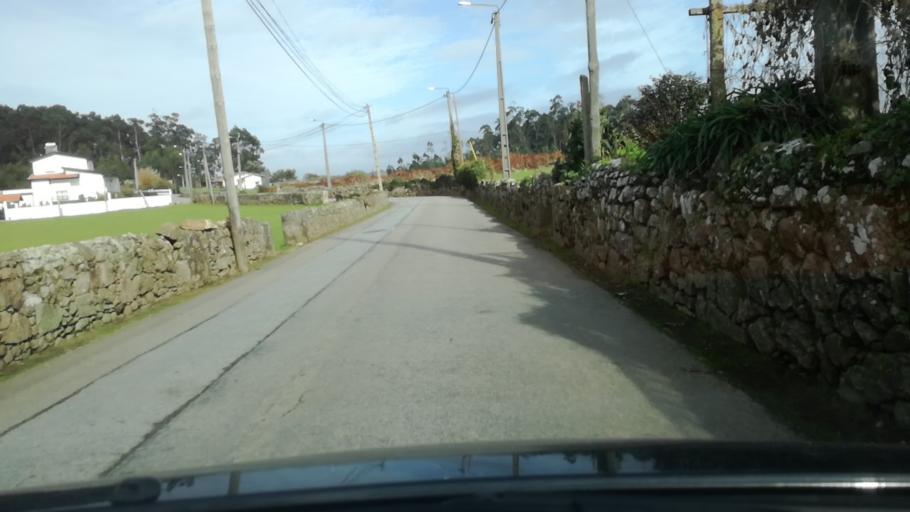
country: PT
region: Porto
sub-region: Maia
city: Gemunde
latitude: 41.2591
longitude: -8.6746
